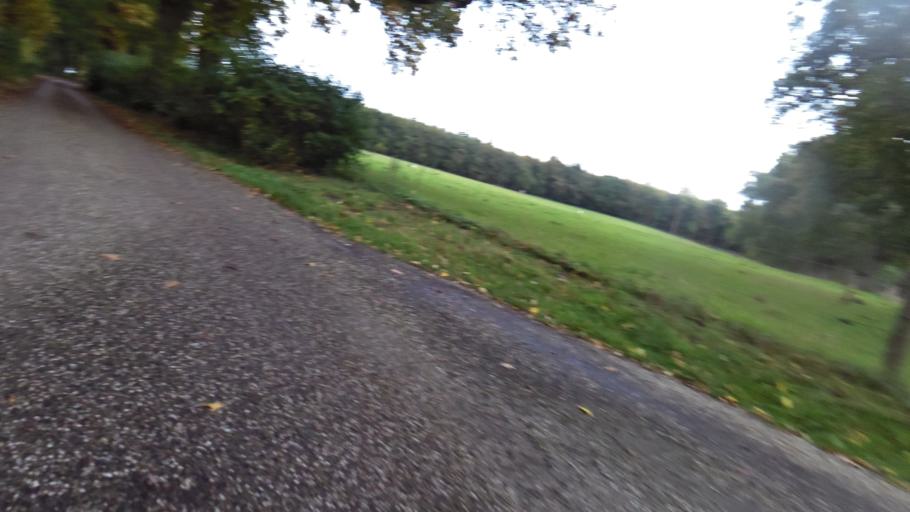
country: NL
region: Gelderland
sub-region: Gemeente Renkum
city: Oosterbeek
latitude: 52.0059
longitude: 5.8411
